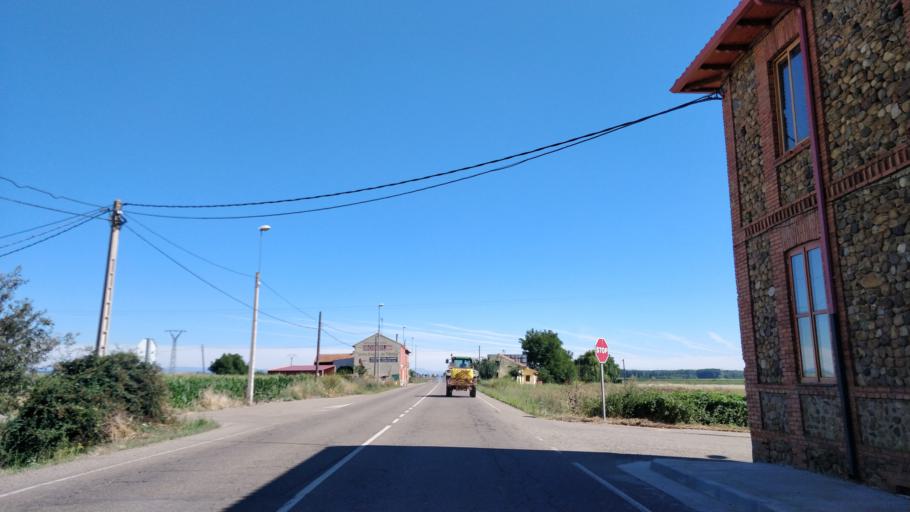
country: ES
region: Castille and Leon
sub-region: Provincia de Leon
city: San Cristobal de la Polantera
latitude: 42.3777
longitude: -5.8889
